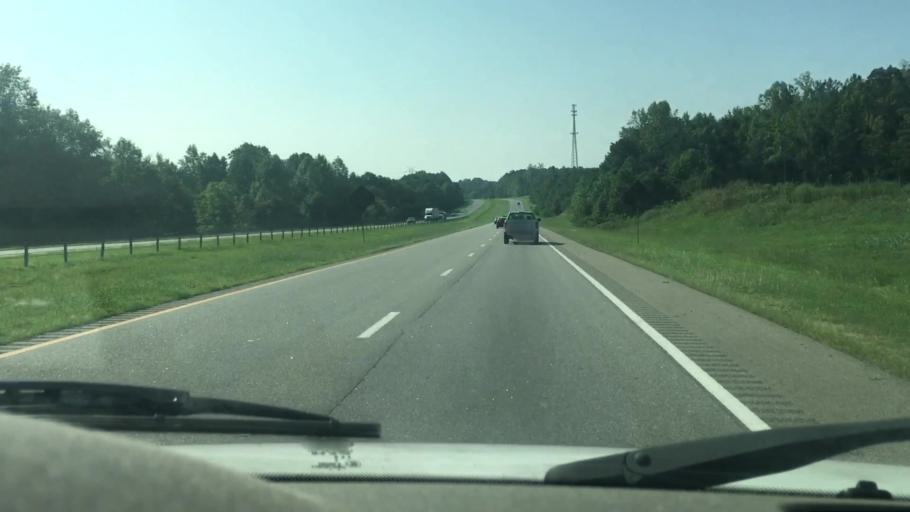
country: US
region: North Carolina
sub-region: Lincoln County
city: Lowesville
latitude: 35.3764
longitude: -80.9980
